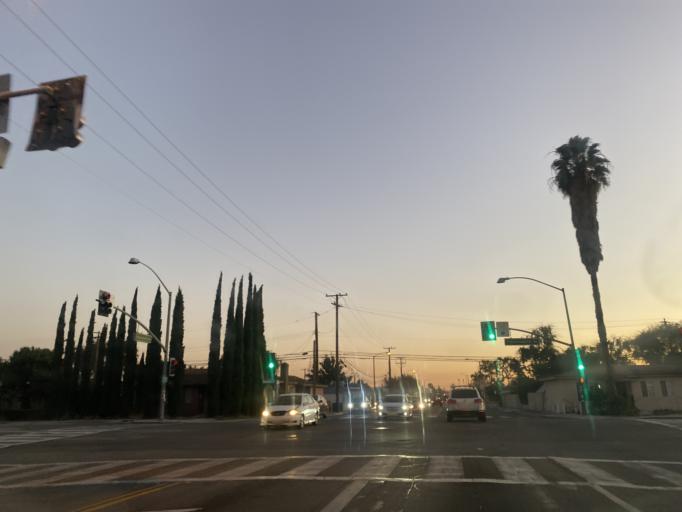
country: US
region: California
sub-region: Orange County
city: Fullerton
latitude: 33.8707
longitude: -117.9070
